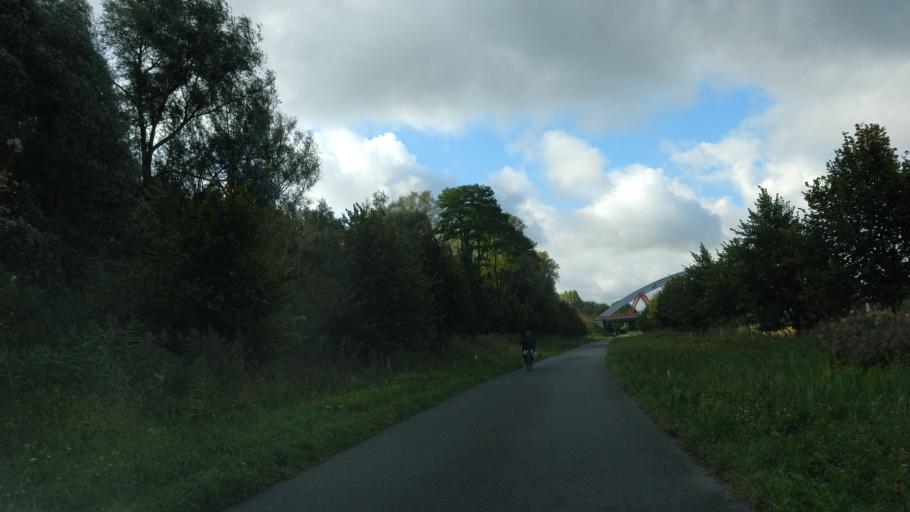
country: BE
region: Flanders
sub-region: Provincie Oost-Vlaanderen
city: Nevele
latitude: 51.0678
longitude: 3.5725
